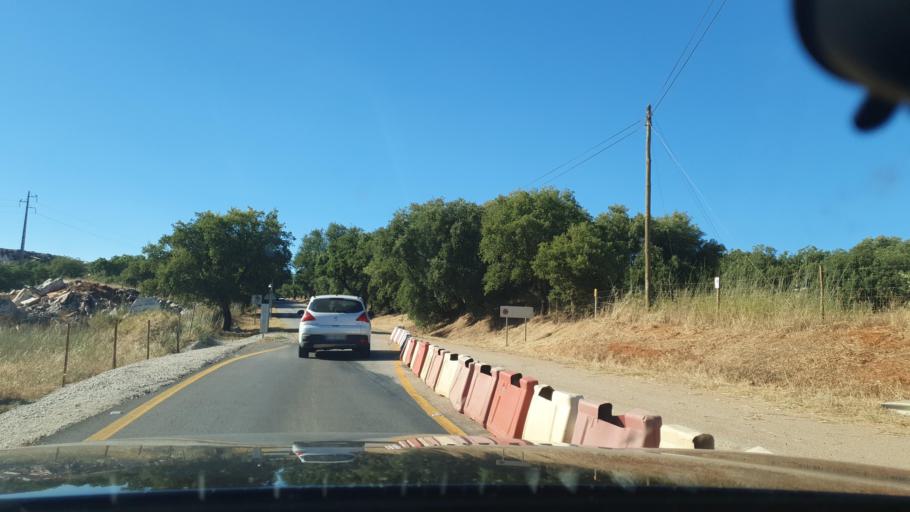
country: PT
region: Evora
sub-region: Vila Vicosa
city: Vila Vicosa
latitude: 38.7414
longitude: -7.4052
